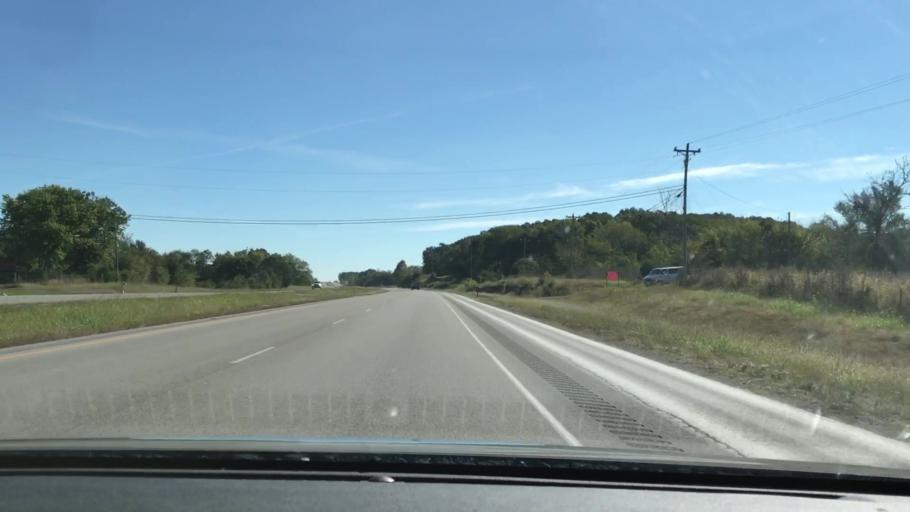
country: US
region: Kentucky
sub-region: Christian County
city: Hopkinsville
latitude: 36.8481
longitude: -87.3336
